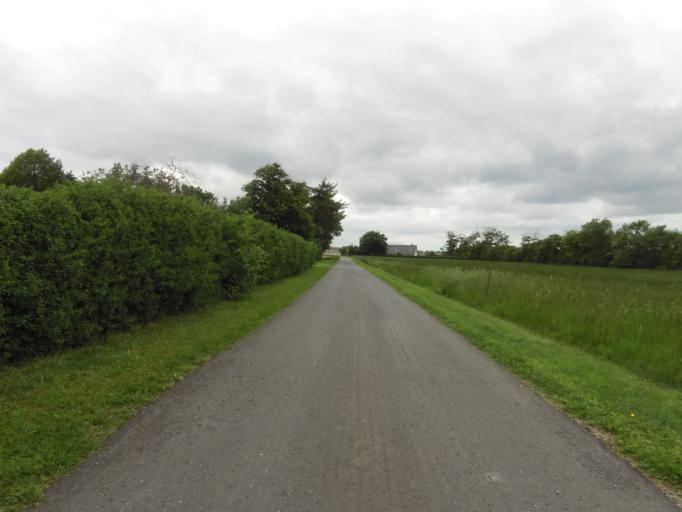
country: DK
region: South Denmark
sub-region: Esbjerg Kommune
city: Ribe
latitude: 55.3104
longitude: 8.7713
